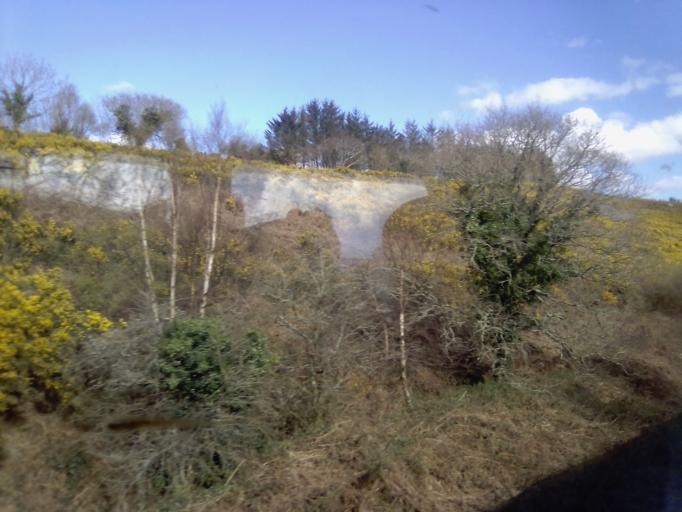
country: IE
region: Munster
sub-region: Ciarrai
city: Cill Airne
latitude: 52.0370
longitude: -9.4518
